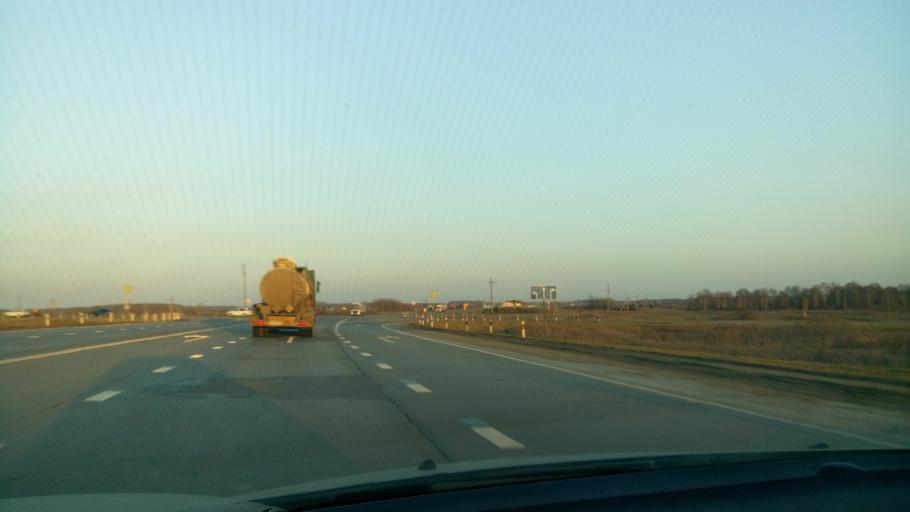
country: RU
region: Sverdlovsk
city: Kamyshlov
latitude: 56.8771
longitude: 62.7104
